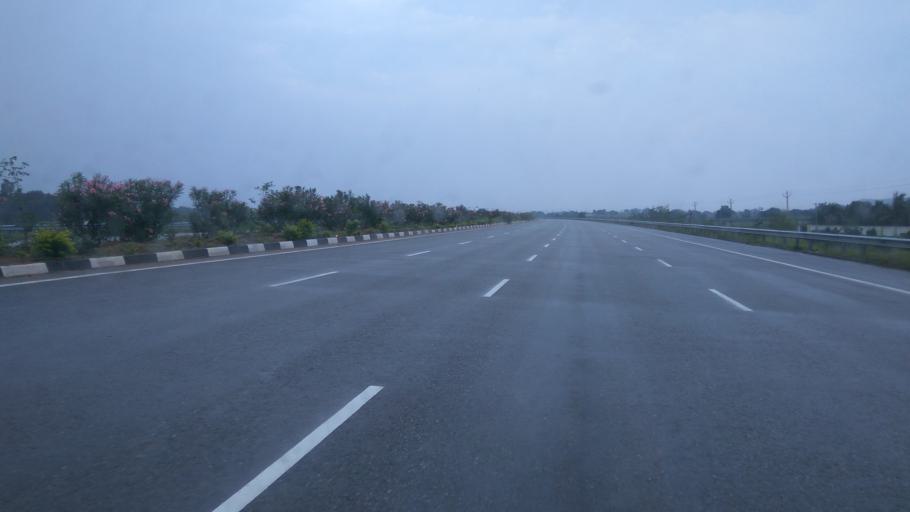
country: IN
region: Telangana
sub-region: Rangareddi
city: Ghatkesar
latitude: 17.4719
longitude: 78.6702
